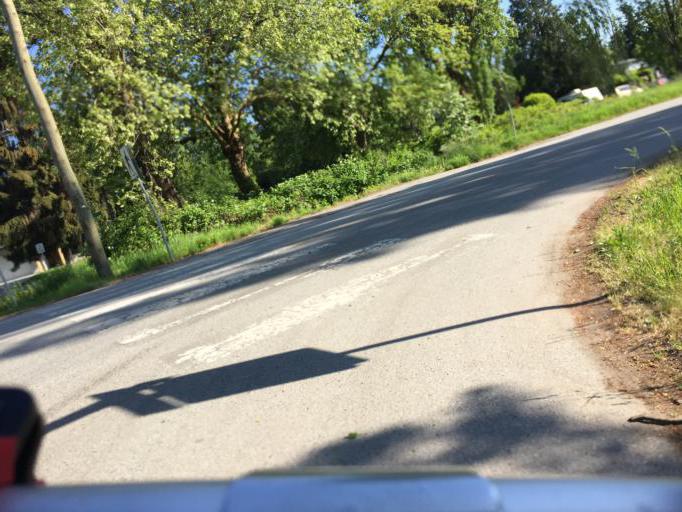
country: CA
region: British Columbia
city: Richmond
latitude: 49.1878
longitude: -123.1470
